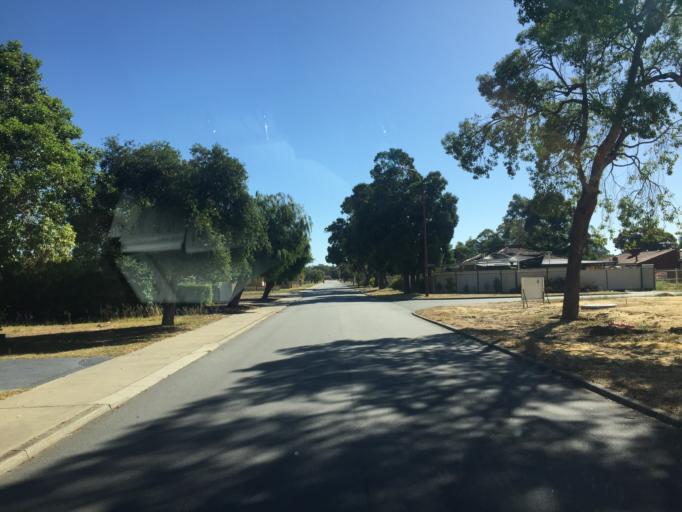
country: AU
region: Western Australia
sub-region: Gosnells
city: Maddington
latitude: -32.0571
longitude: 116.0004
